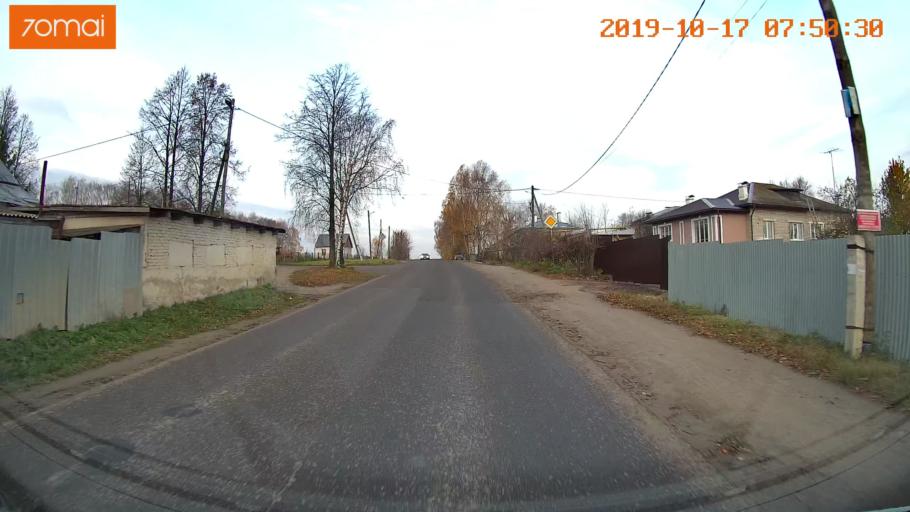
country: RU
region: Vladimir
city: Yur'yev-Pol'skiy
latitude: 56.4840
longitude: 39.6648
